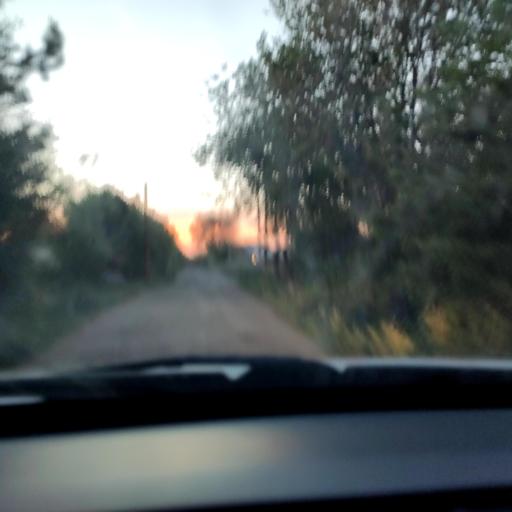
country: RU
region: Samara
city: Samara
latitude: 53.1309
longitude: 50.2397
